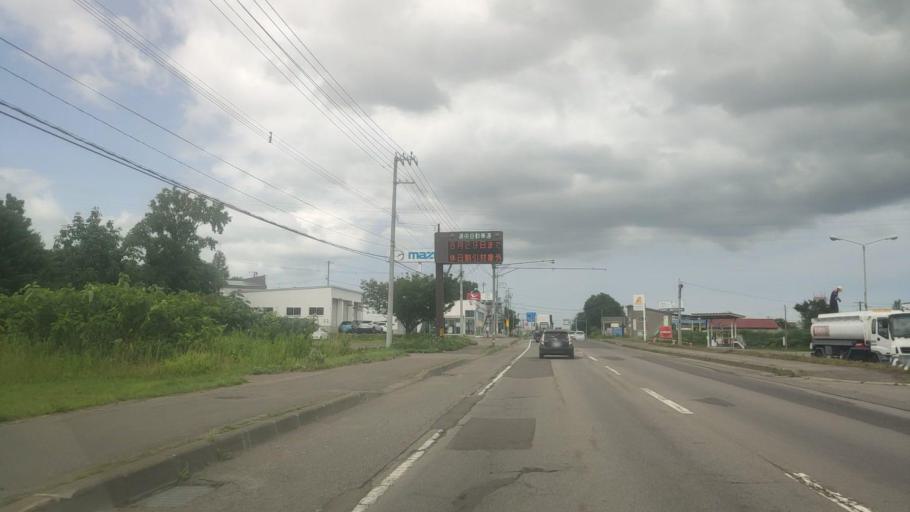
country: JP
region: Hokkaido
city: Nanae
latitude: 42.0911
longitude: 140.5792
